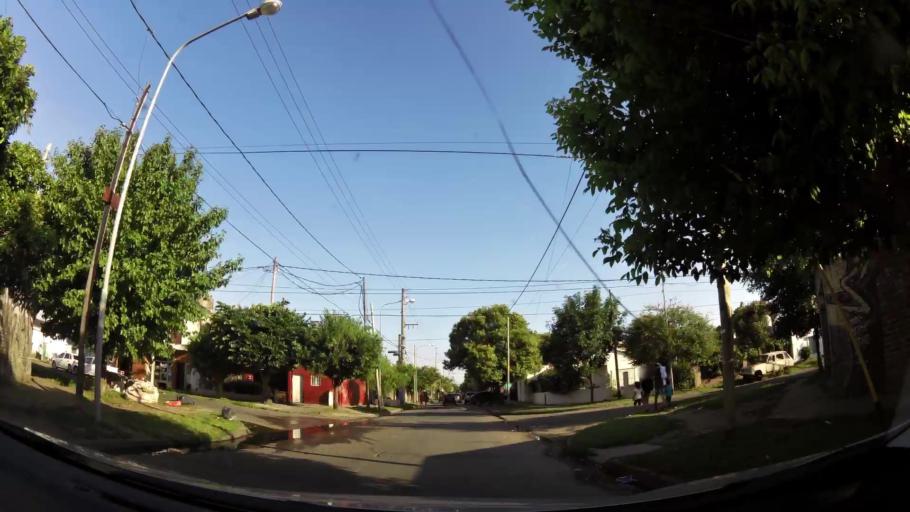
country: AR
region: Buenos Aires
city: Santa Catalina - Dique Lujan
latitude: -34.4649
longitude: -58.6640
